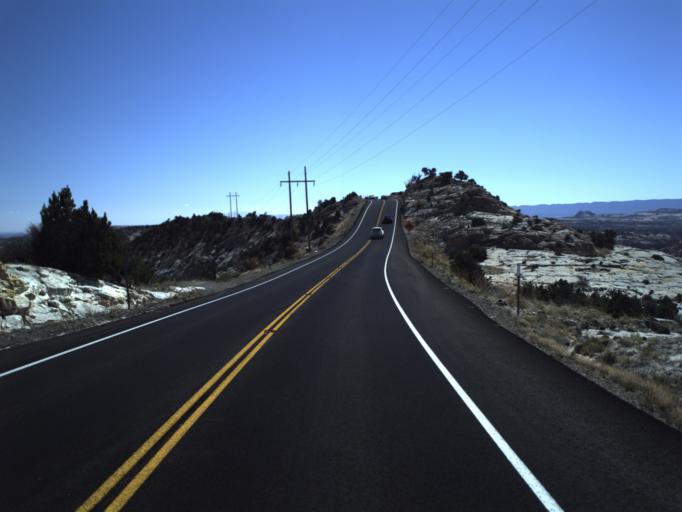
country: US
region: Utah
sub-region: Wayne County
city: Loa
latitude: 37.8336
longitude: -111.4162
